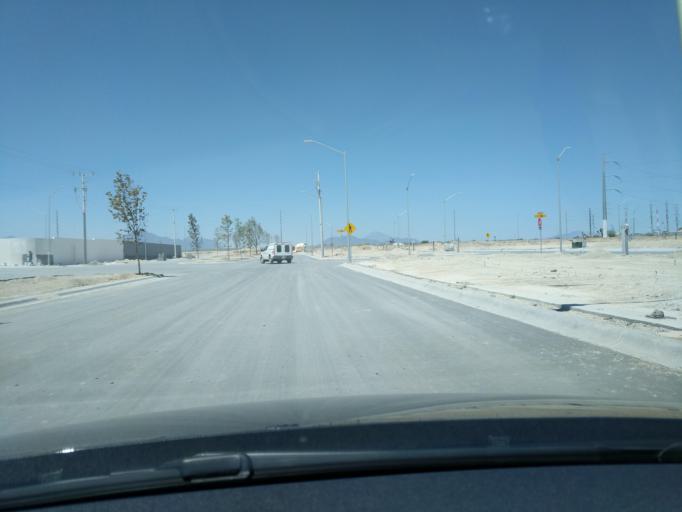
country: MX
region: Nuevo Leon
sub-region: Apodaca
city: Artemio Trevino
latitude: 25.8441
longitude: -100.1429
